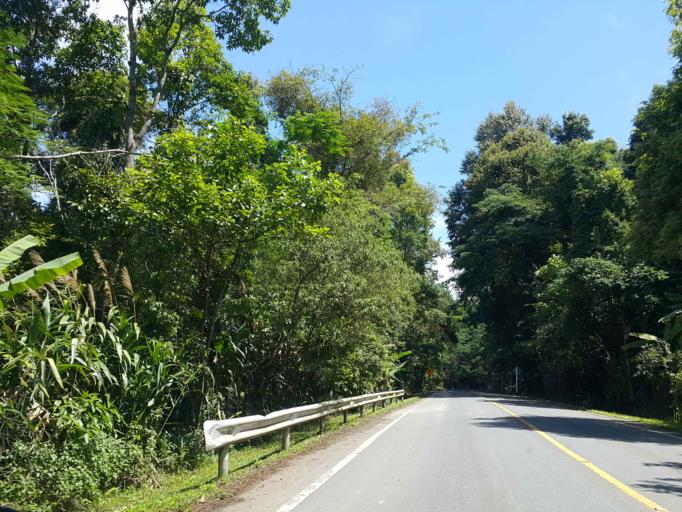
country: TH
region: Chiang Mai
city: Mae Chaem
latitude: 18.5427
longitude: 98.5309
